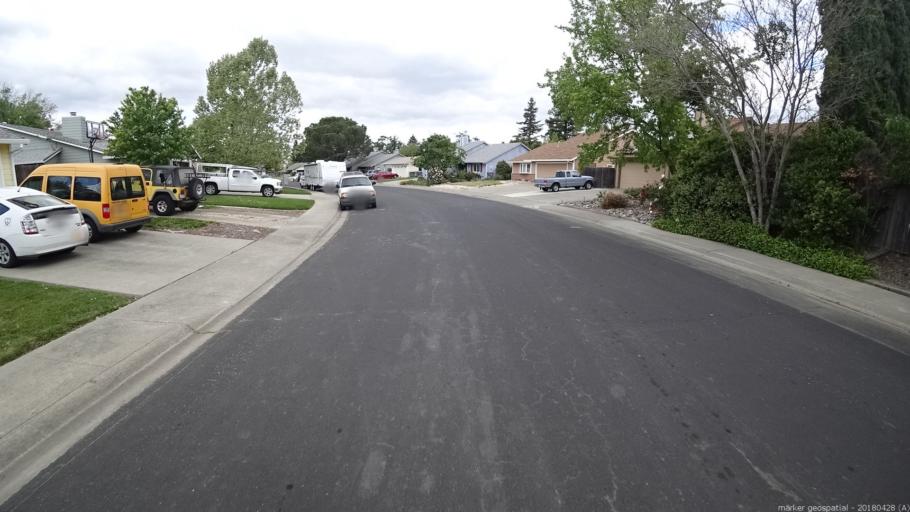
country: US
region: California
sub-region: Yolo County
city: West Sacramento
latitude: 38.5502
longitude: -121.5567
